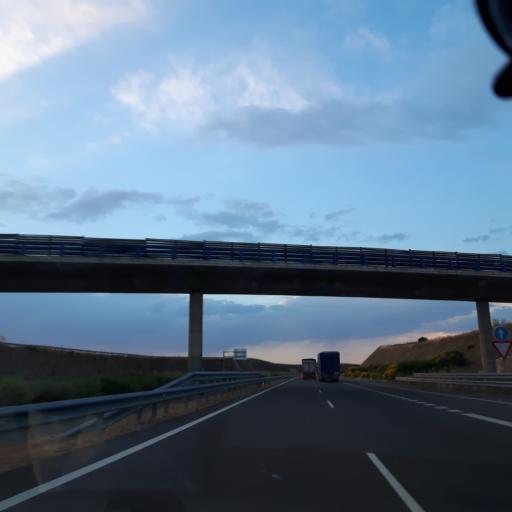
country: ES
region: Castille and Leon
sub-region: Provincia de Salamanca
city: Mozarbez
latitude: 40.8671
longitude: -5.6513
